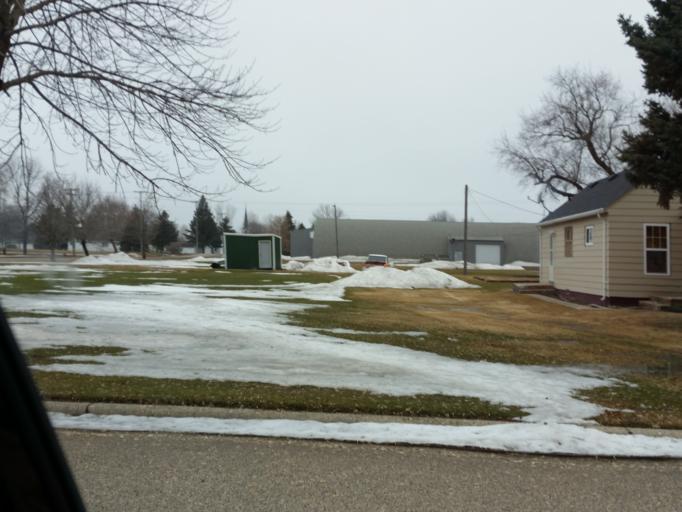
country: US
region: North Dakota
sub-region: Walsh County
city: Grafton
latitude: 48.6164
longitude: -97.4449
